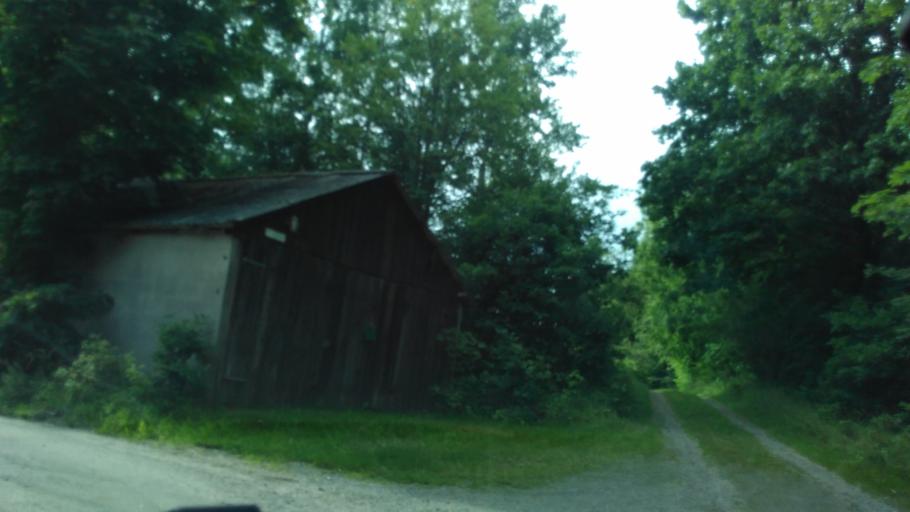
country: SE
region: Vaestra Goetaland
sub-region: Alingsas Kommun
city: Alingsas
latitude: 57.9912
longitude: 12.6048
